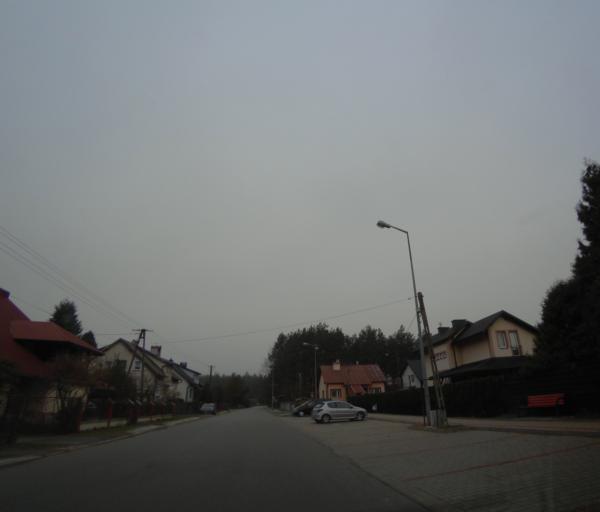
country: PL
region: Subcarpathian Voivodeship
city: Nowa Sarzyna
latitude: 50.3134
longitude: 22.3418
